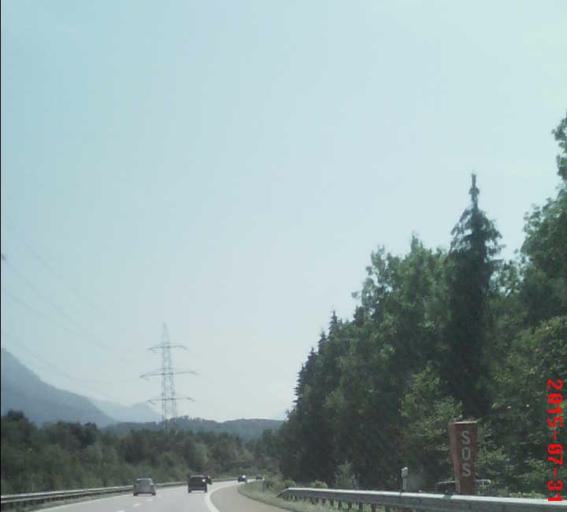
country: CH
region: Saint Gallen
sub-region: Wahlkreis Werdenberg
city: Sennwald
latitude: 47.2662
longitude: 9.5282
